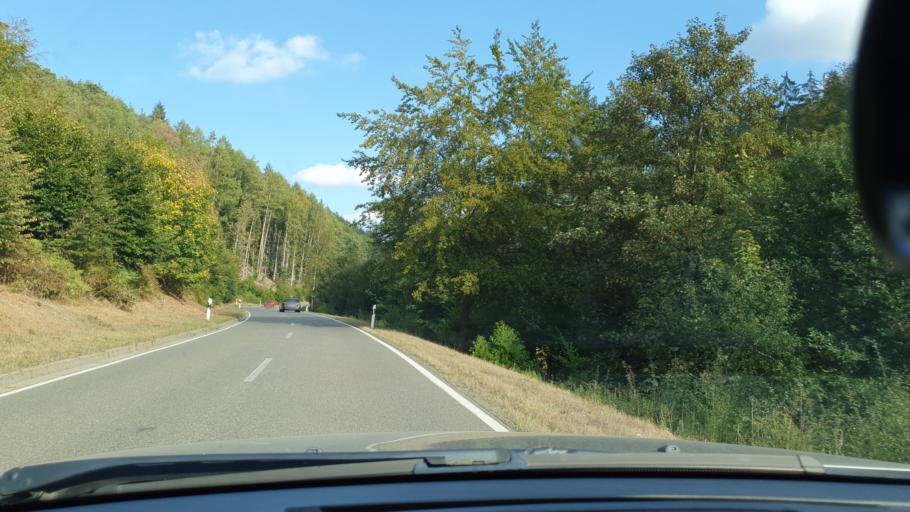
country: DE
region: Rheinland-Pfalz
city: Stelzenberg
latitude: 49.3684
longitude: 7.7135
